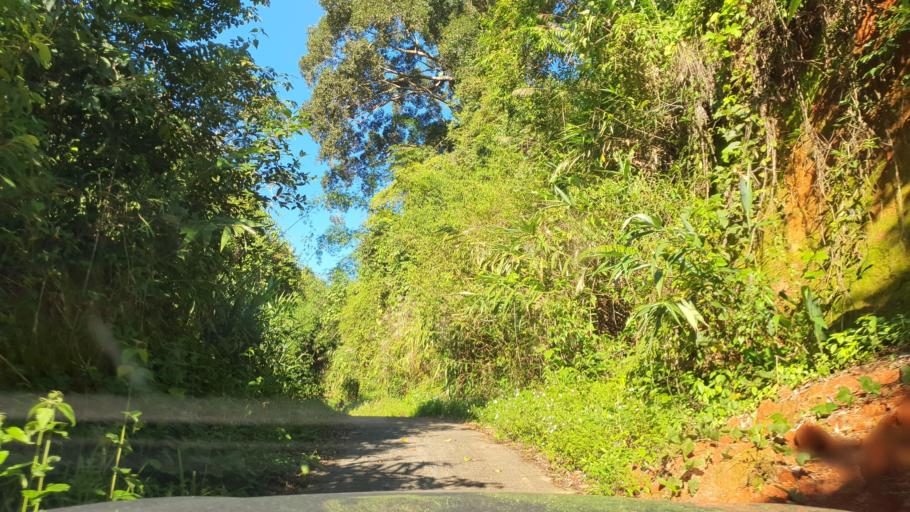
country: TH
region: Chiang Mai
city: Mae On
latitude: 18.8157
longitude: 99.3424
